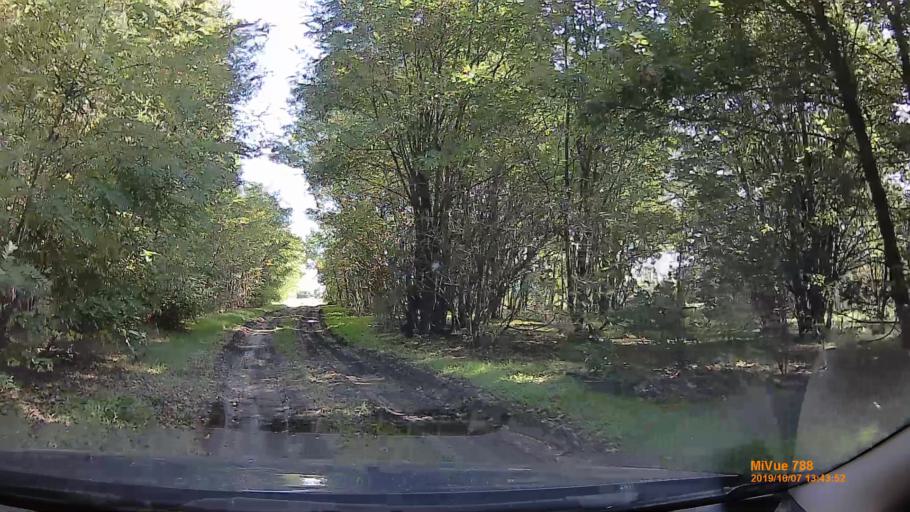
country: HU
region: Jasz-Nagykun-Szolnok
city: Cserkeszolo
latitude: 46.8810
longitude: 20.1988
